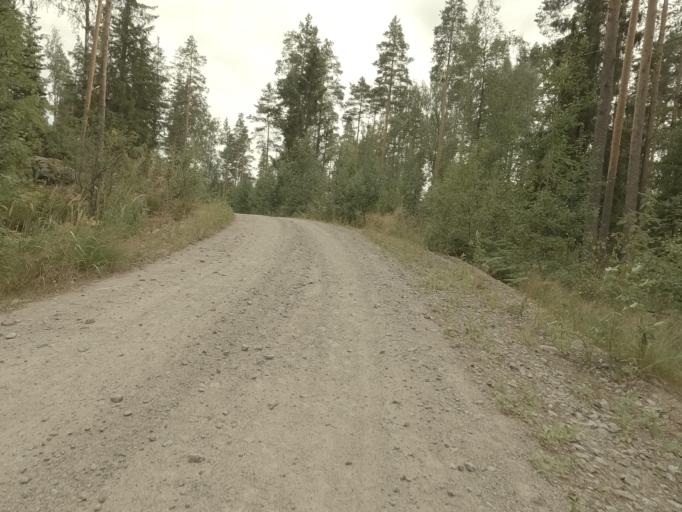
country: RU
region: Leningrad
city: Kamennogorsk
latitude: 60.9792
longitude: 29.1713
